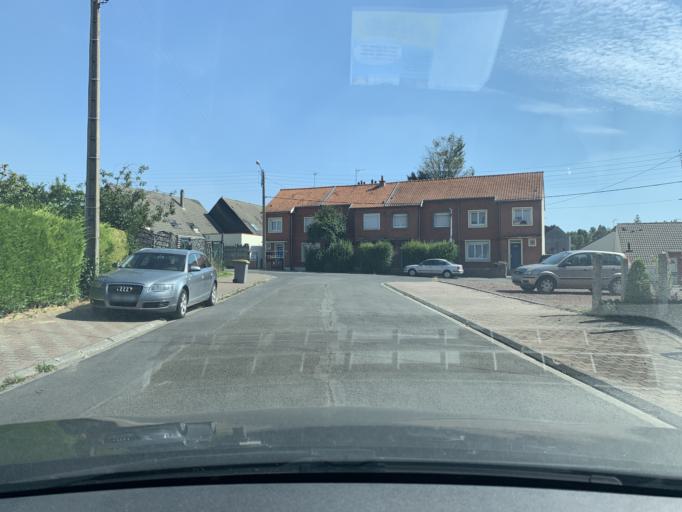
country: FR
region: Nord-Pas-de-Calais
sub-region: Departement du Nord
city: Cambrai
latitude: 50.1584
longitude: 3.2455
